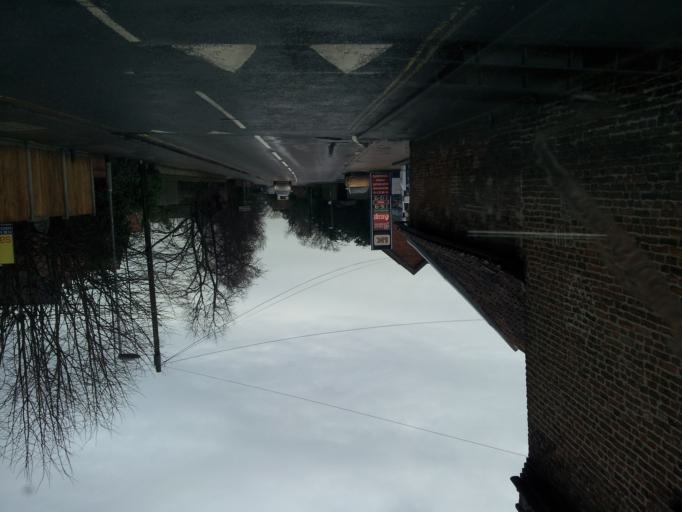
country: GB
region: England
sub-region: Norfolk
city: Brundall
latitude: 52.6212
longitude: 1.4420
